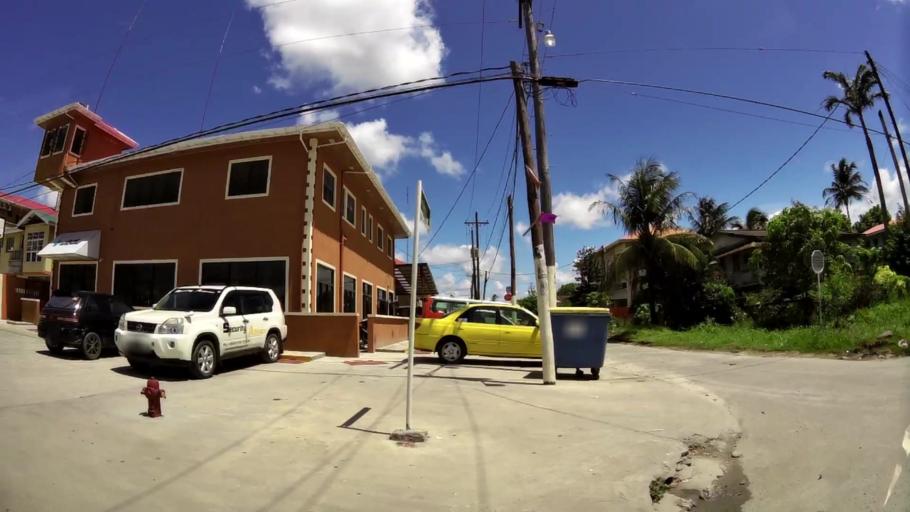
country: GY
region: Demerara-Mahaica
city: Georgetown
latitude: 6.7882
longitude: -58.1481
